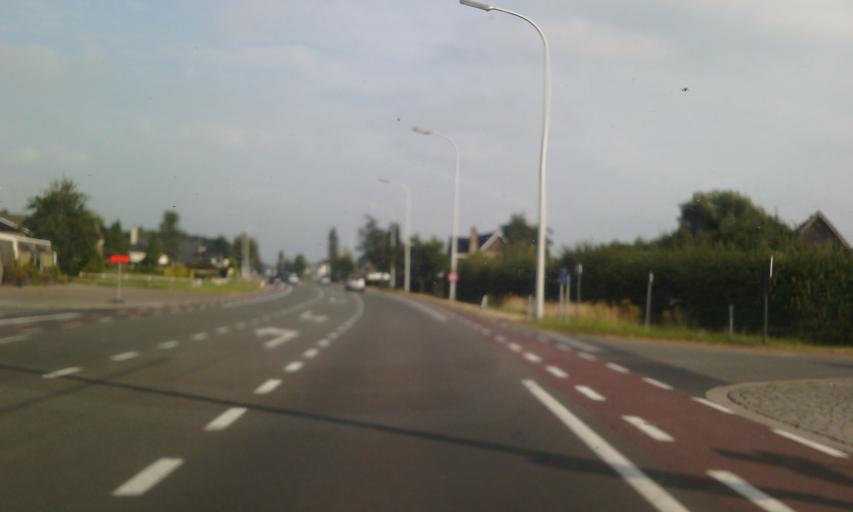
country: BE
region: Flanders
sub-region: Provincie Oost-Vlaanderen
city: Lovendegem
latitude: 51.1087
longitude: 3.6152
